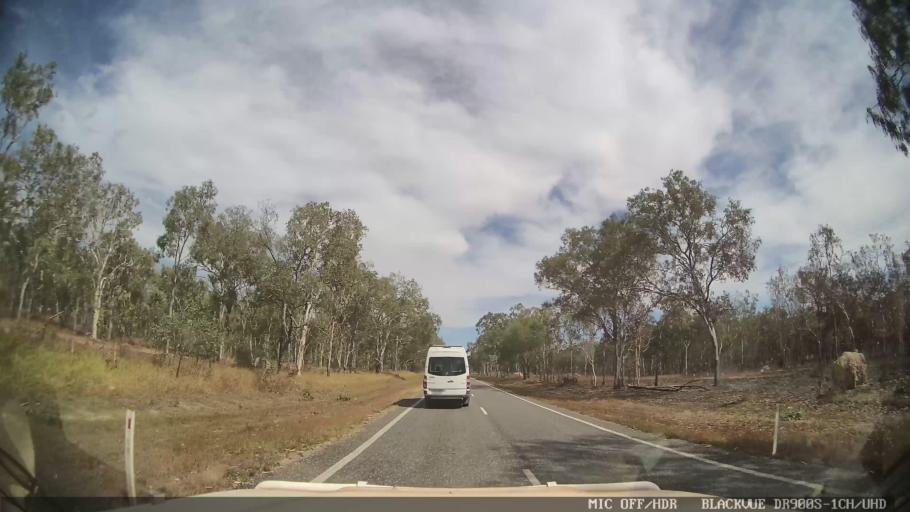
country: AU
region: Queensland
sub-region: Cairns
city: Port Douglas
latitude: -16.7255
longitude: 145.3528
